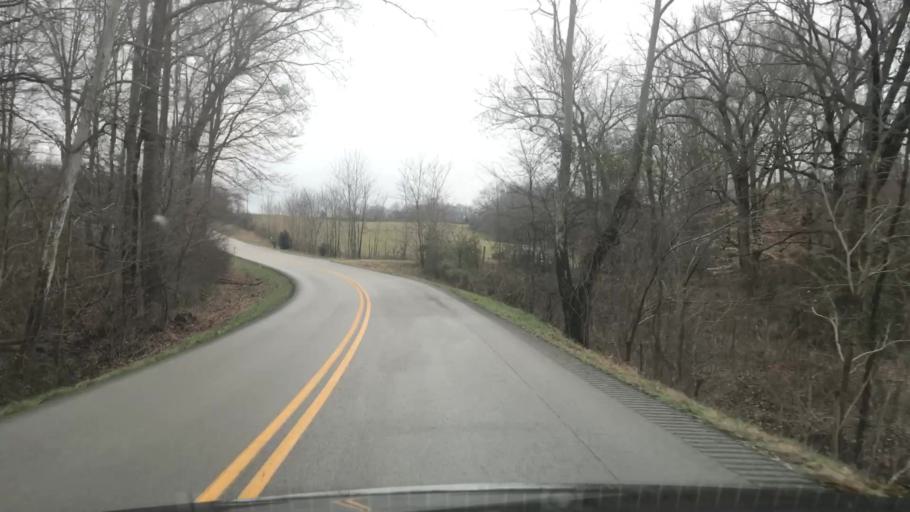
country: US
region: Kentucky
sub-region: Monroe County
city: Tompkinsville
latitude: 36.8478
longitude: -85.7693
